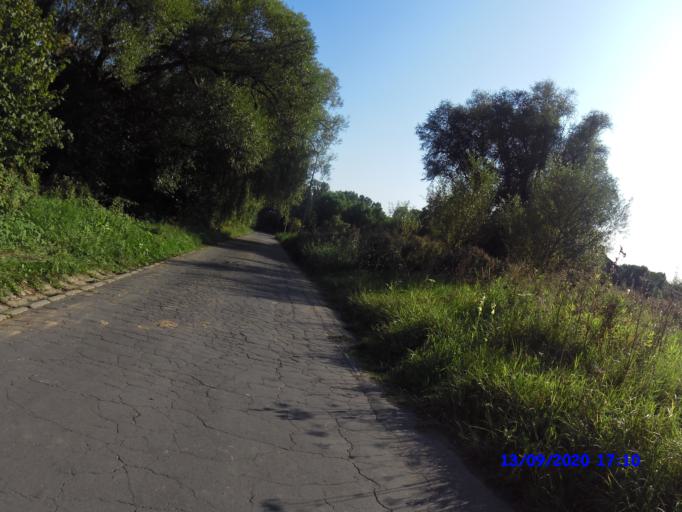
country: BE
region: Flanders
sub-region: Provincie Vlaams-Brabant
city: Dilbeek
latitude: 50.8306
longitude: 4.2616
